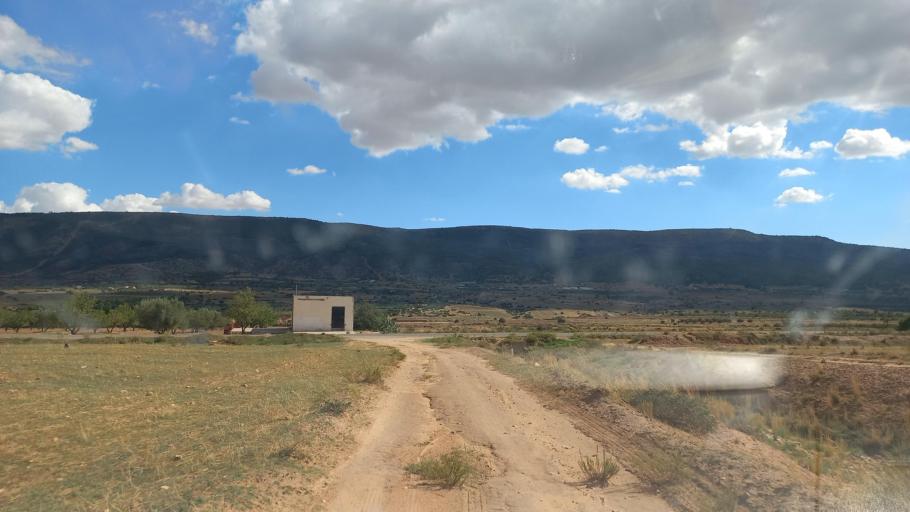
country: TN
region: Al Qasrayn
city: Kasserine
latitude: 35.3696
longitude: 8.8849
